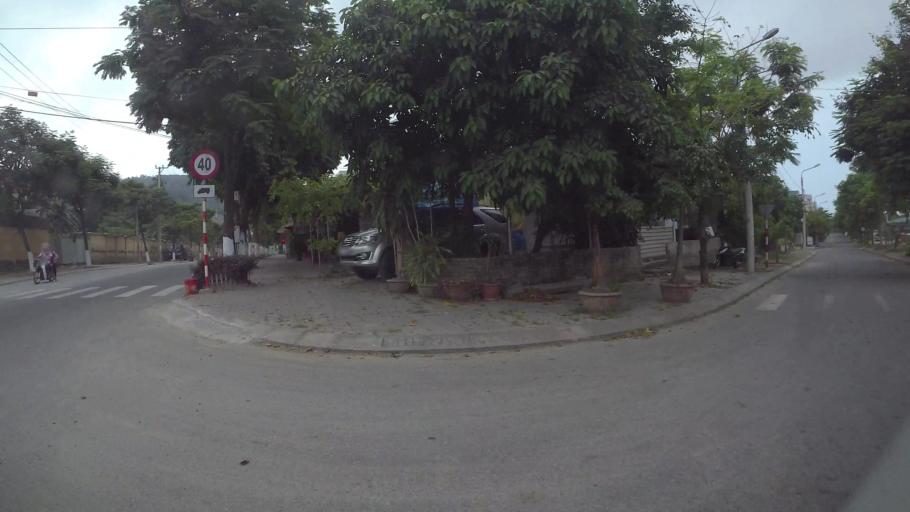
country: VN
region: Da Nang
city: Cam Le
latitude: 16.0348
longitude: 108.1754
